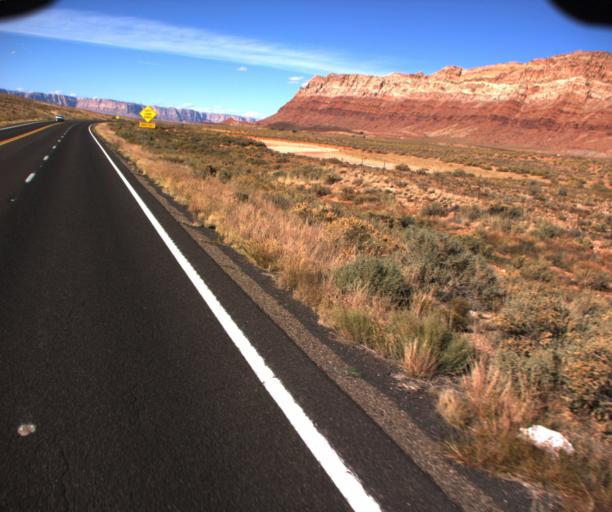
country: US
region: Arizona
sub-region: Coconino County
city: LeChee
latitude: 36.5680
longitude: -111.6396
